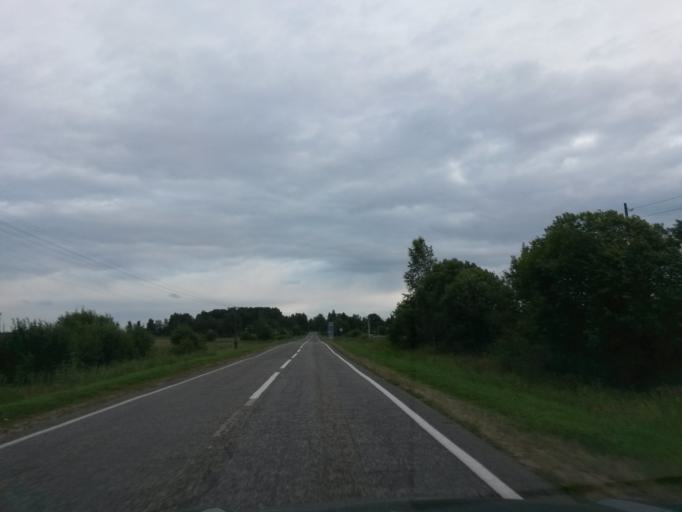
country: RU
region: Jaroslavl
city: Tutayev
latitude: 57.9026
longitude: 39.5237
